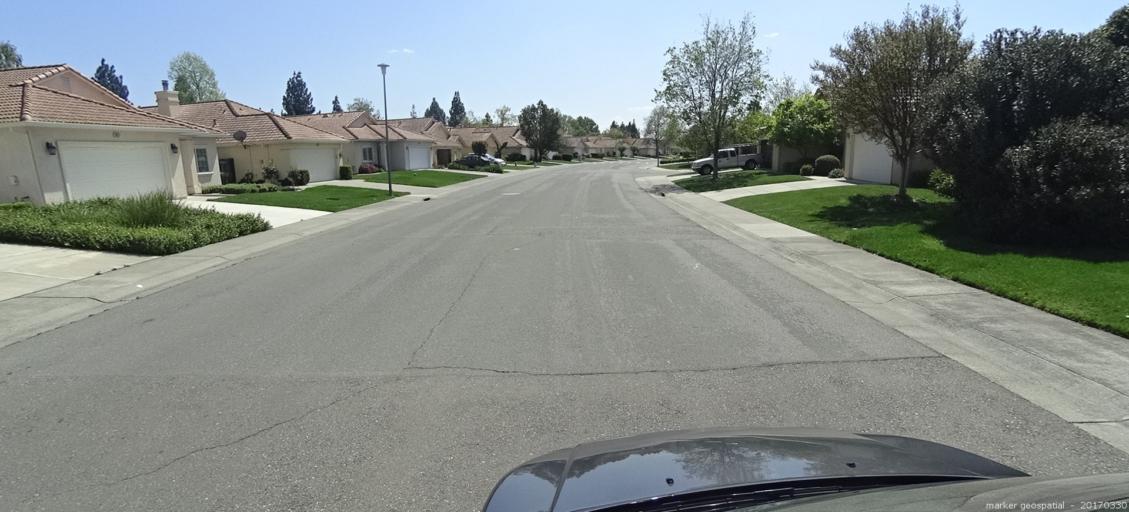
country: US
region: California
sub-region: Sacramento County
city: Florin
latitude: 38.4656
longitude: -121.4185
